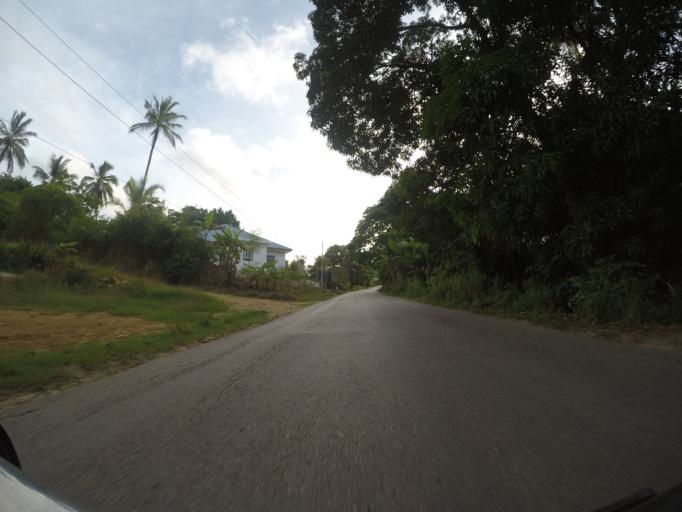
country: TZ
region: Pemba South
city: Chake Chake
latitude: -5.2779
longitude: 39.7686
